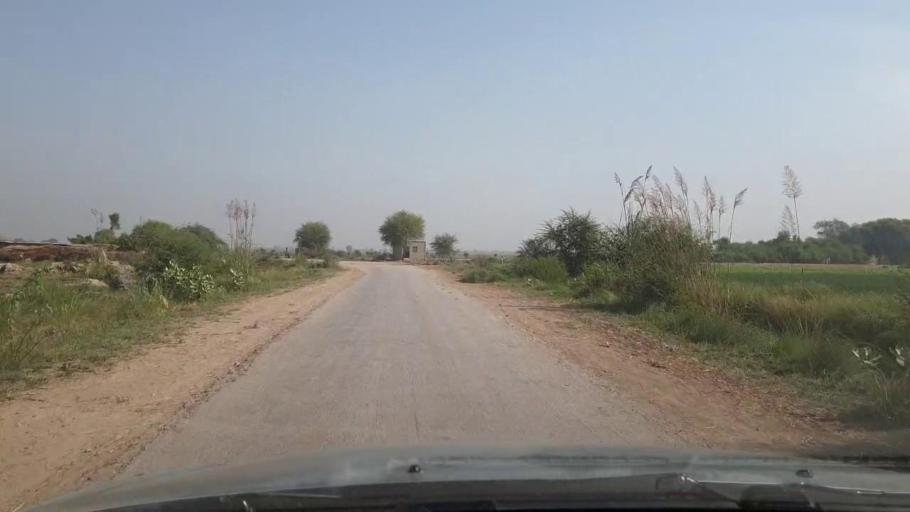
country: PK
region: Sindh
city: Tando Jam
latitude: 25.2855
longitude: 68.5187
